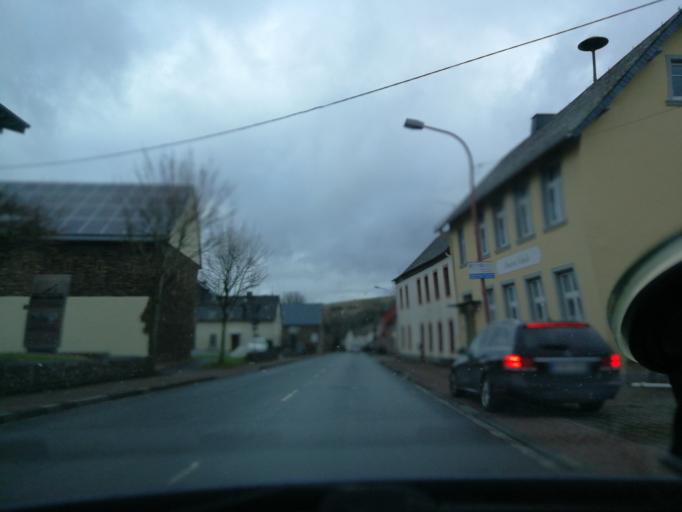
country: DE
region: Rheinland-Pfalz
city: Dreis-Bruck
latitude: 50.2630
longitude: 6.7921
